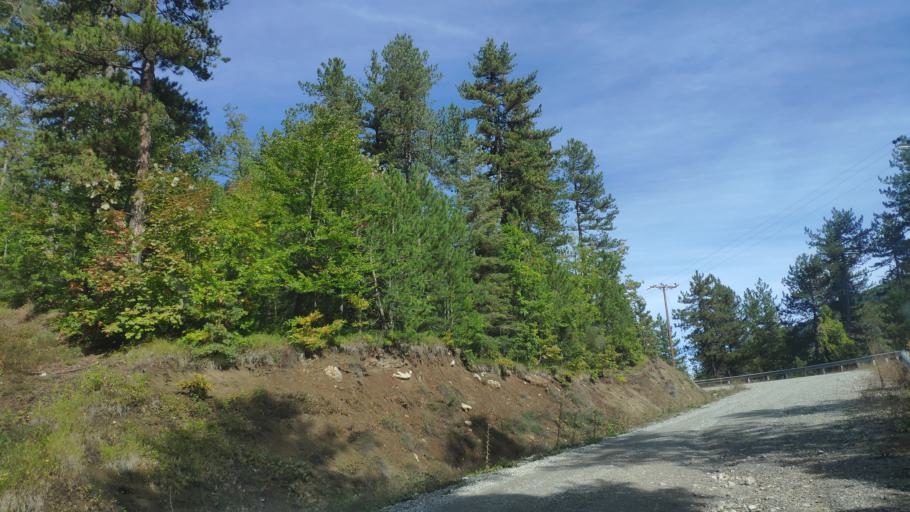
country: AL
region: Korce
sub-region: Rrethi i Devollit
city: Miras
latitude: 40.4147
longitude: 20.8710
